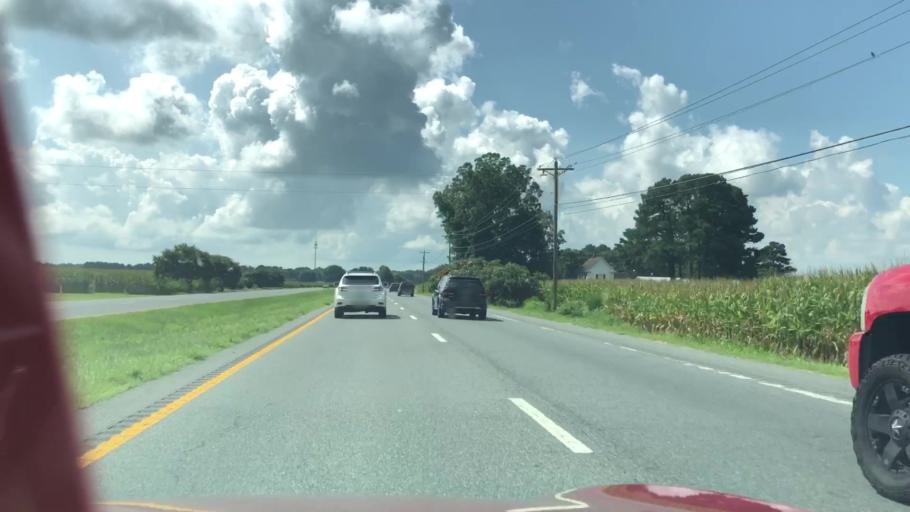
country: US
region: Virginia
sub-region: Accomack County
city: Wattsville
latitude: 37.8646
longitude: -75.5576
